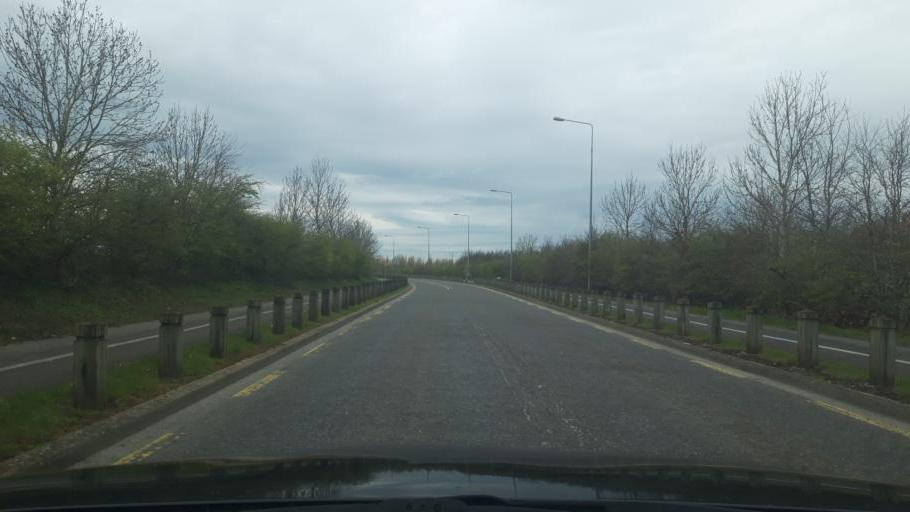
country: IE
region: Leinster
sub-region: Kildare
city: Celbridge
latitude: 53.3582
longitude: -6.5243
